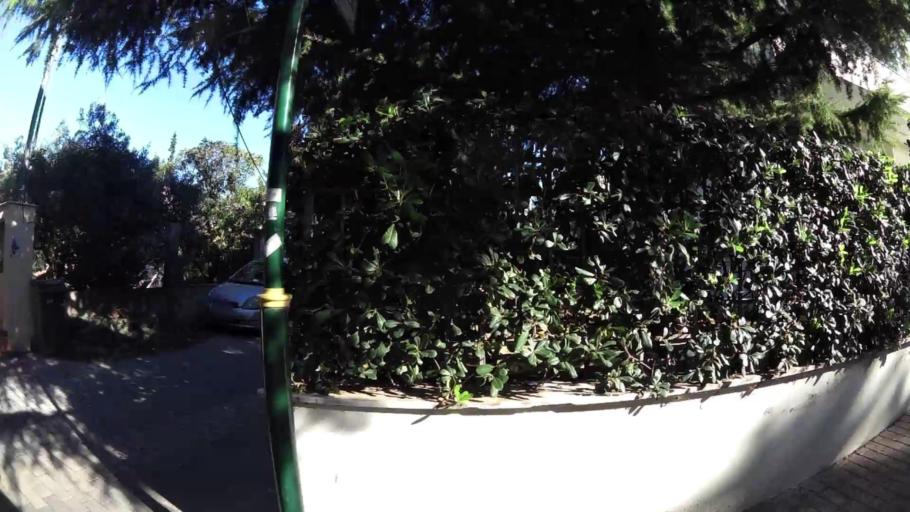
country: GR
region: Attica
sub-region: Nomarchia Athinas
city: Nea Erythraia
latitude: 38.0962
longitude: 23.8221
